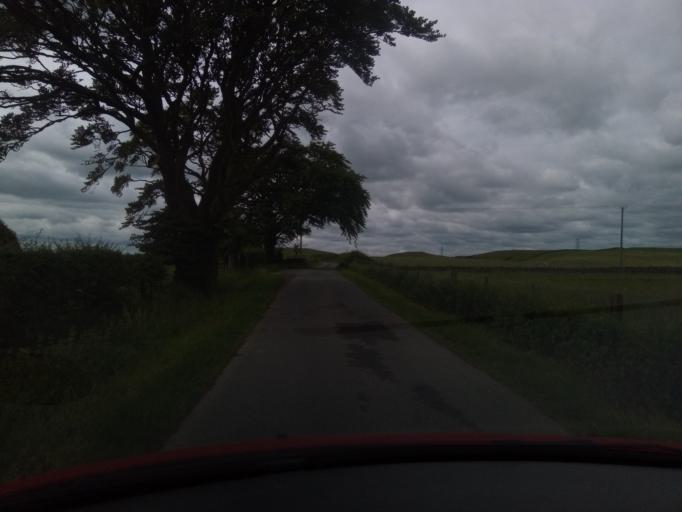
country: GB
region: Scotland
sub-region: The Scottish Borders
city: Hawick
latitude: 55.4464
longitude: -2.8056
